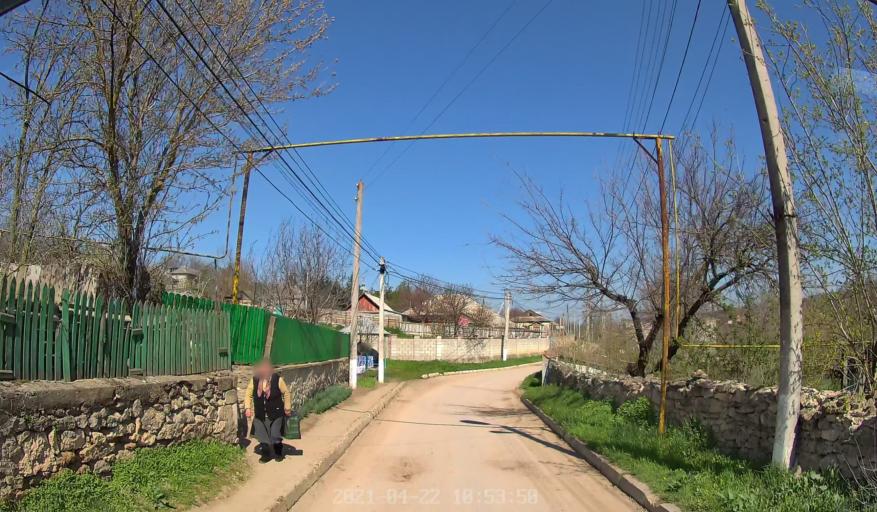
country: MD
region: Chisinau
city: Ciorescu
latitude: 47.1672
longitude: 28.9511
